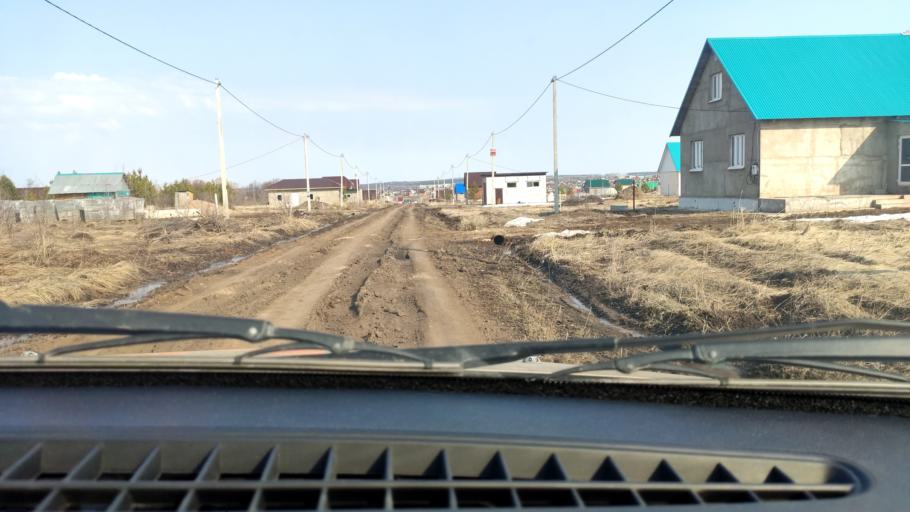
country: RU
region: Bashkortostan
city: Iglino
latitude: 54.7941
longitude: 56.4032
